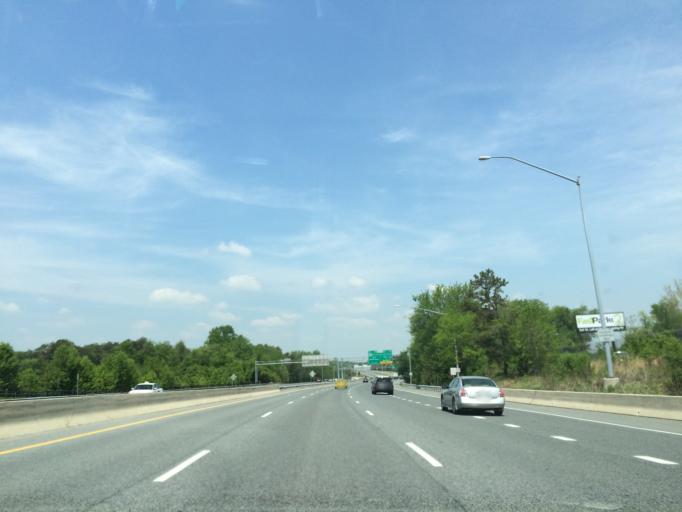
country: US
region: Maryland
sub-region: Howard County
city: Elkridge
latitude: 39.1911
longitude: -76.6864
